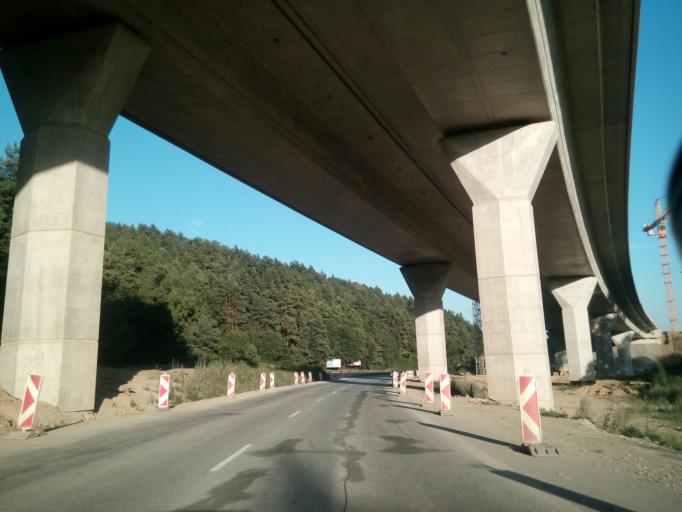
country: SK
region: Presovsky
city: Sabinov
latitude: 49.0195
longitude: 21.0360
